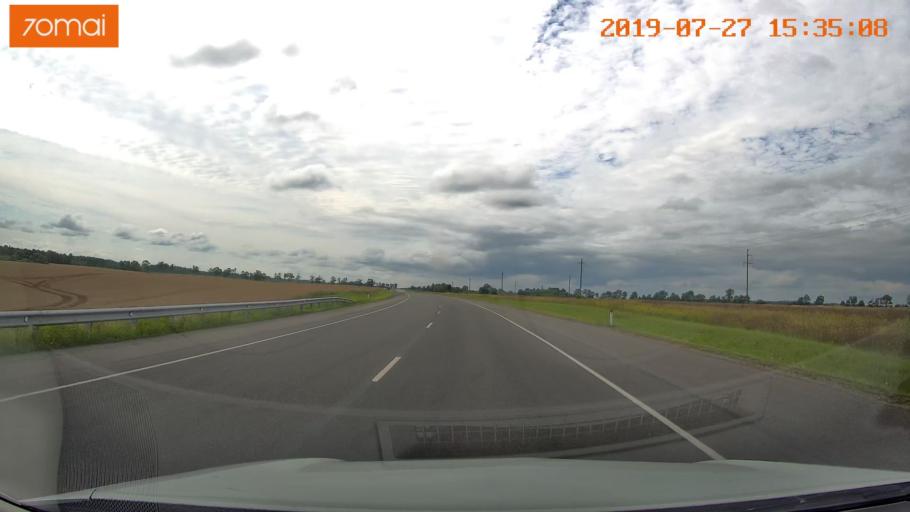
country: RU
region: Kaliningrad
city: Nesterov
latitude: 54.6140
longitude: 22.4052
